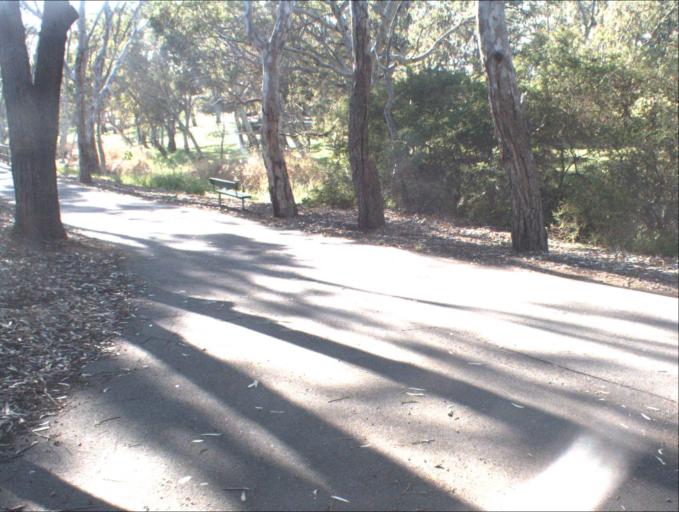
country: AU
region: South Australia
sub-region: Port Adelaide Enfield
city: Klemzig
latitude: -34.8741
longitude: 138.6482
